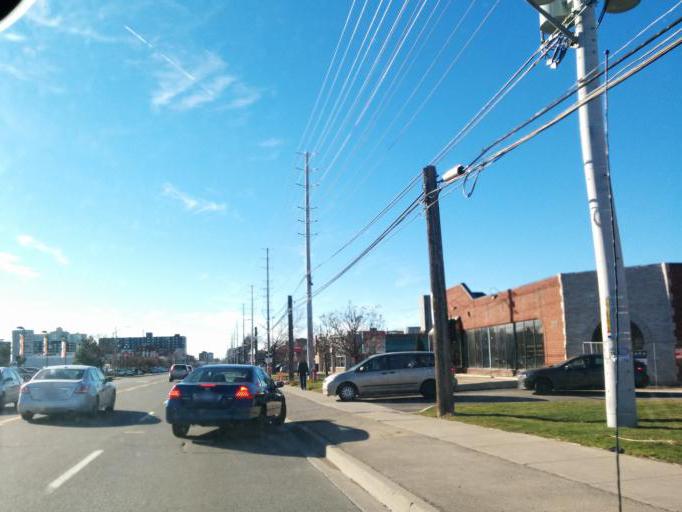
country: CA
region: Ontario
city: Mississauga
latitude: 43.5871
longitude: -79.6087
